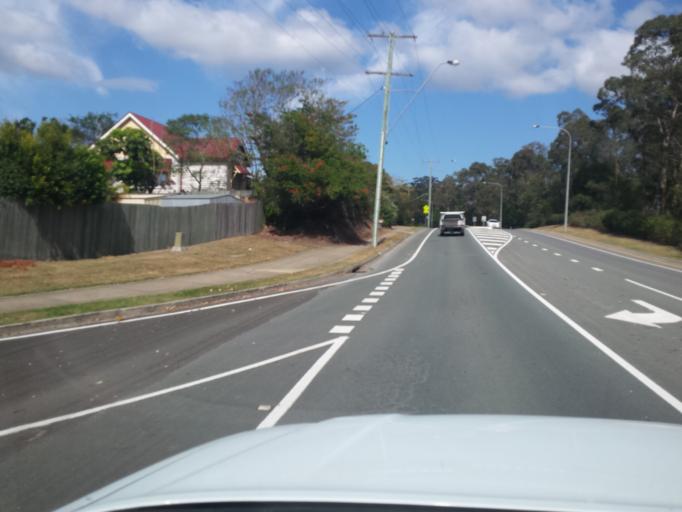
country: AU
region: Queensland
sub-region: Moreton Bay
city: Ferny Hills
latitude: -27.3819
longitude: 152.9452
